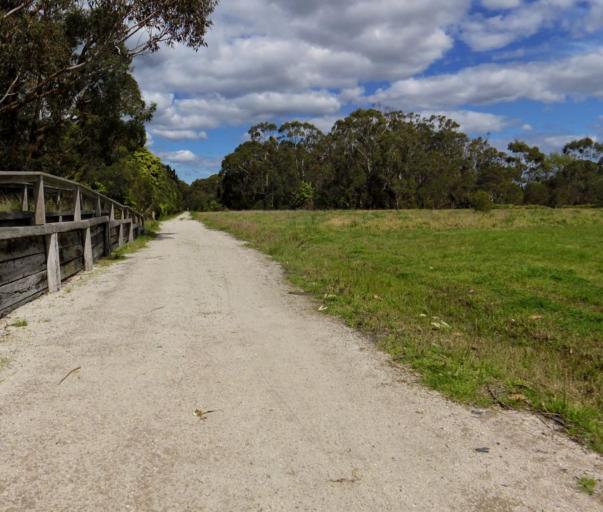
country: AU
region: Victoria
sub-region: Bass Coast
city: North Wonthaggi
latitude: -38.6535
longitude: 146.0280
